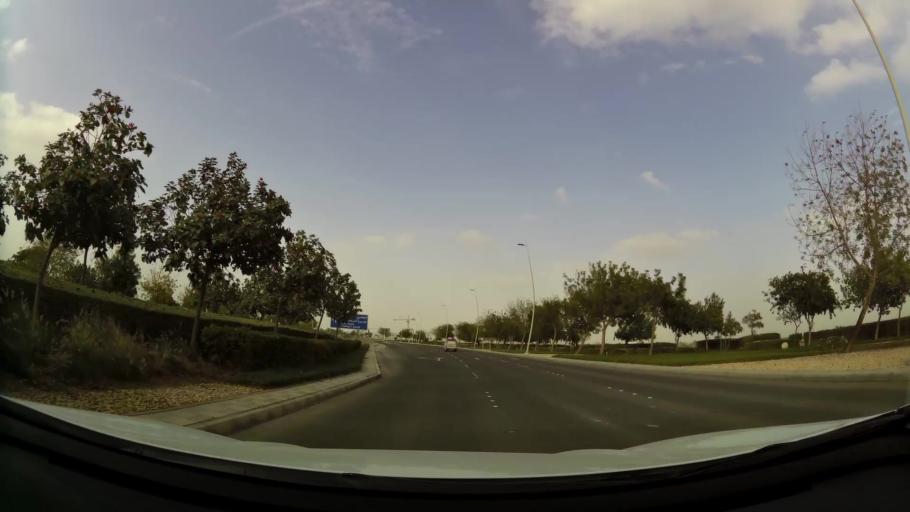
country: AE
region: Abu Dhabi
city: Abu Dhabi
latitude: 24.4893
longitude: 54.6312
